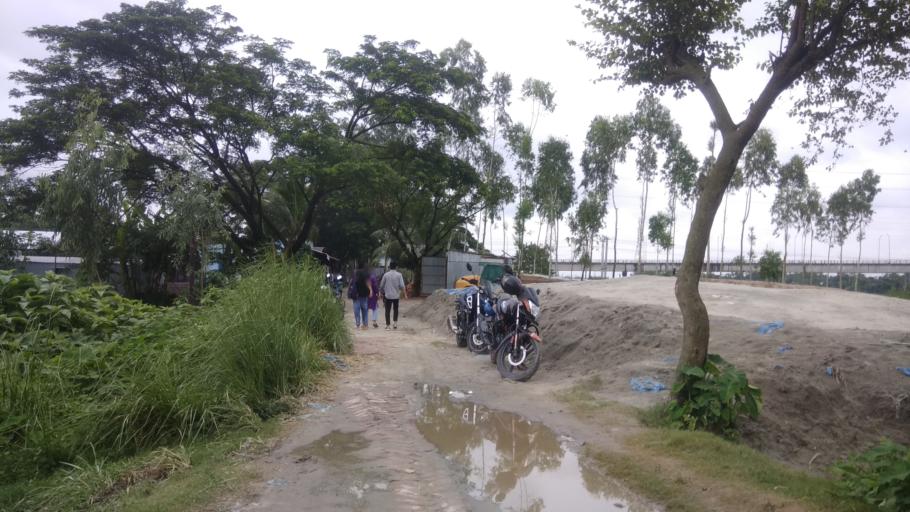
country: BD
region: Dhaka
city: Azimpur
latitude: 23.6713
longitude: 90.2879
